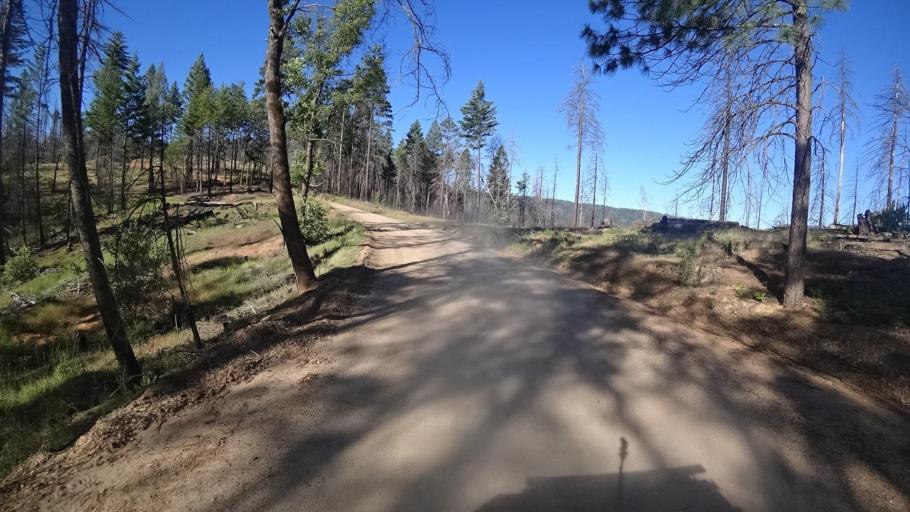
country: US
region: California
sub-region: Lake County
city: Upper Lake
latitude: 39.3892
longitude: -122.9799
